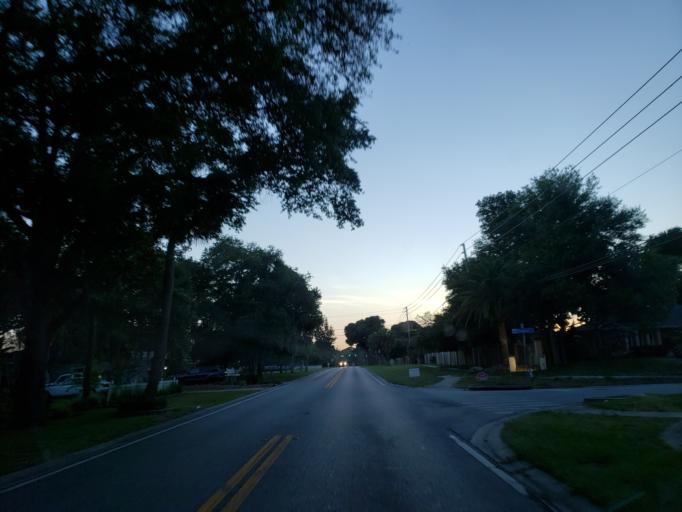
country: US
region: Florida
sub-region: Pinellas County
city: Harbor Bluffs
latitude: 27.9096
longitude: -82.8185
